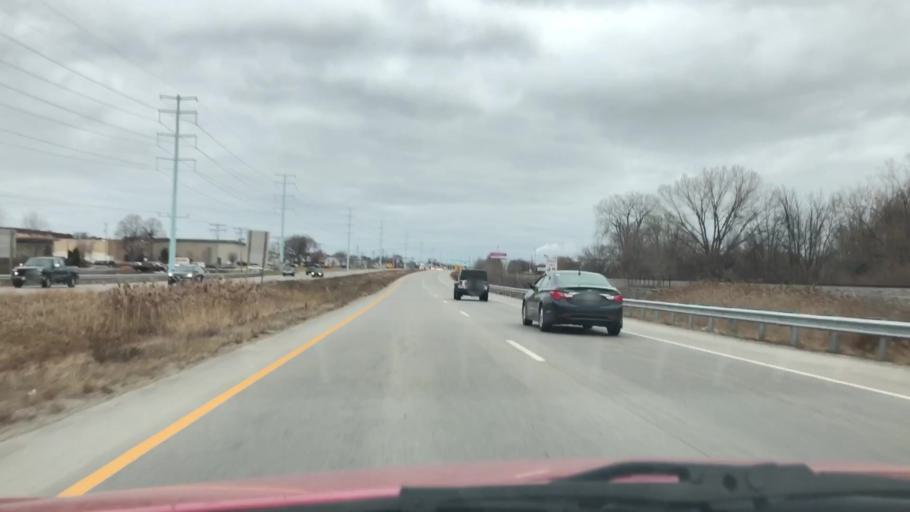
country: US
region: Wisconsin
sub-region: Brown County
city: Ashwaubenon
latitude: 44.4816
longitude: -88.0568
